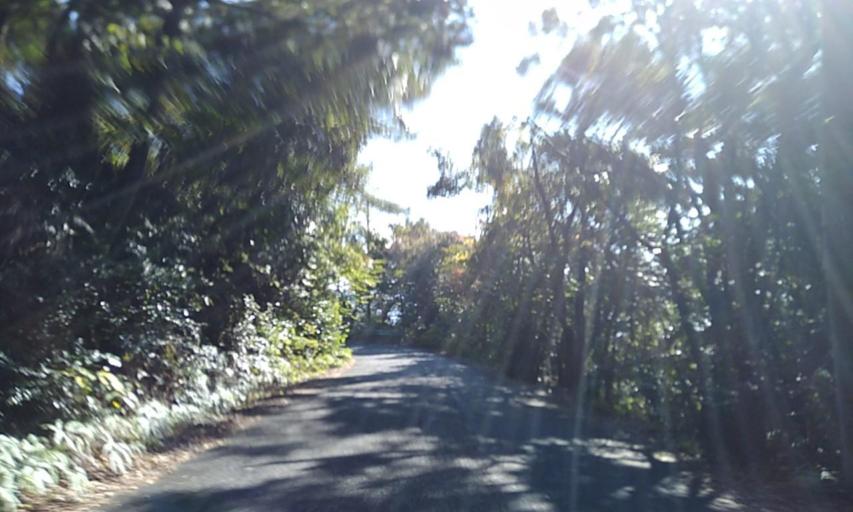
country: JP
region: Shizuoka
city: Hamakita
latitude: 34.8179
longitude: 137.6429
